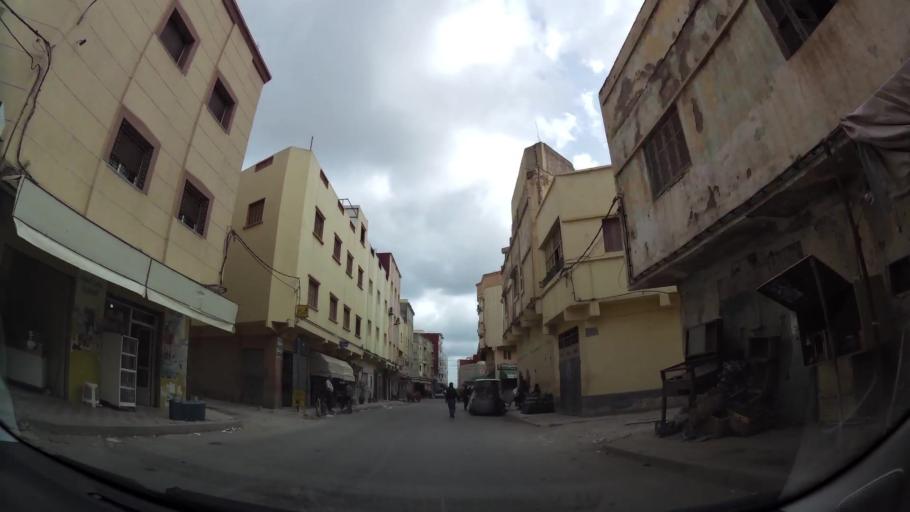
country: MA
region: Oriental
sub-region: Nador
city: Nador
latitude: 35.1682
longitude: -2.9417
